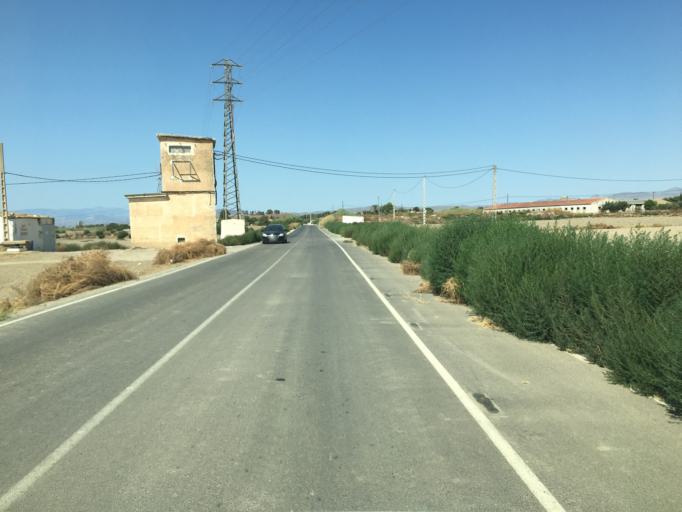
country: ES
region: Andalusia
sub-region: Provincia de Almeria
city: Huercal-Overa
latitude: 37.4199
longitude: -1.9081
